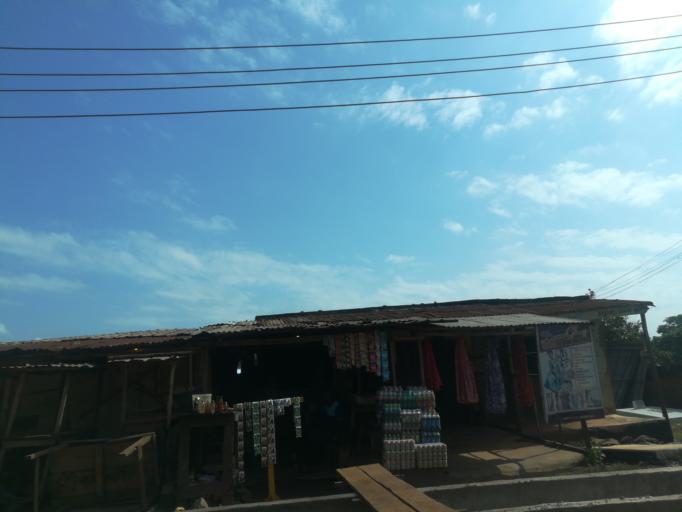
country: NG
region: Oyo
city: Ibadan
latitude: 7.4182
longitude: 3.9765
